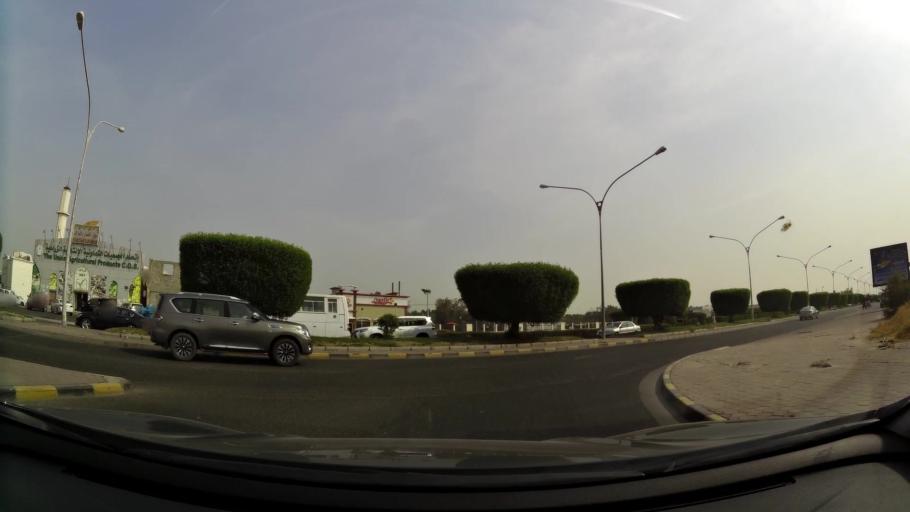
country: KW
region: Al Asimah
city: Ar Rabiyah
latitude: 29.2953
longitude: 47.9388
